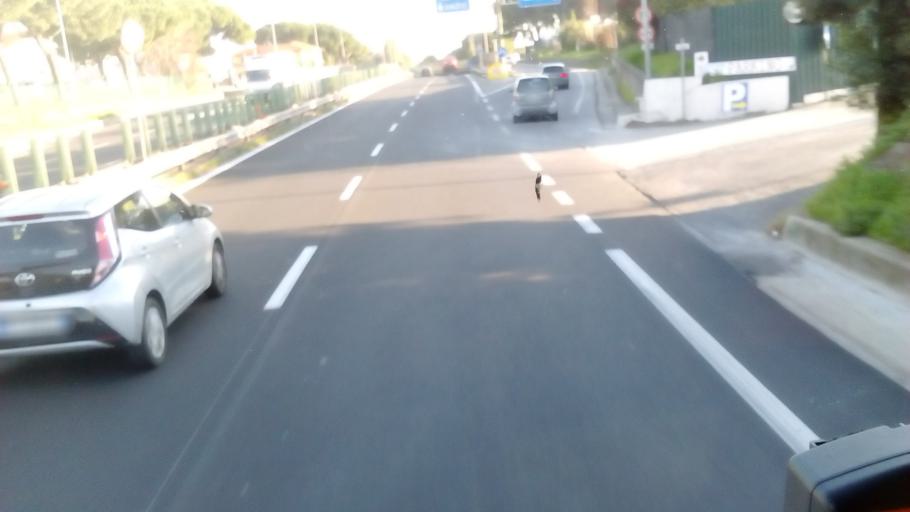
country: IT
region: Latium
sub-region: Citta metropolitana di Roma Capitale
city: Ciampino
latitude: 41.7906
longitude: 12.5941
